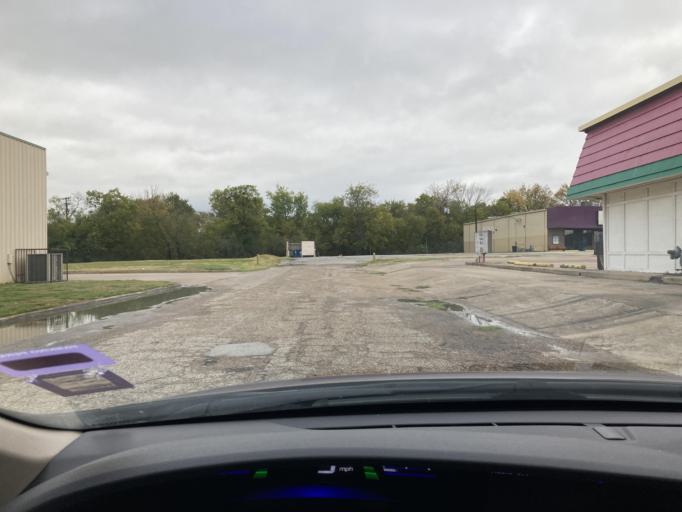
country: US
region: Texas
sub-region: Navarro County
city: Corsicana
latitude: 32.0826
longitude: -96.4809
